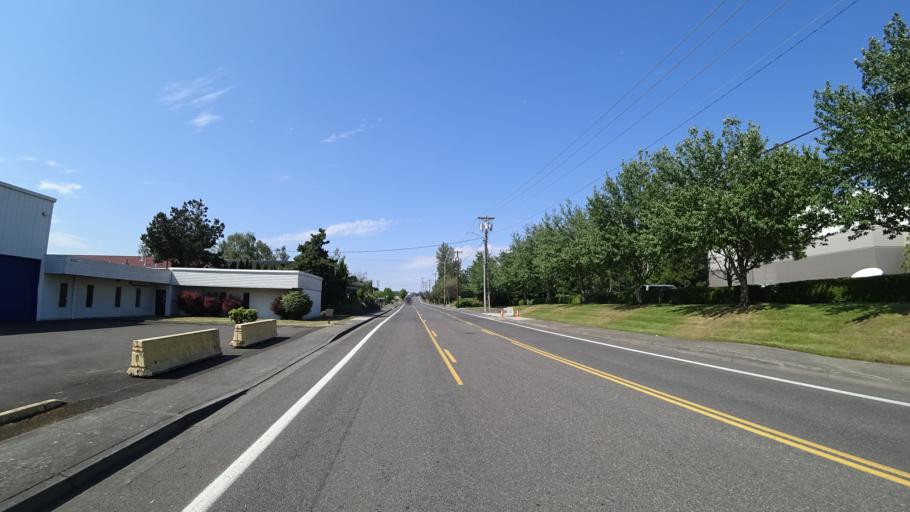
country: US
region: Oregon
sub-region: Multnomah County
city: Fairview
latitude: 45.5600
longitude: -122.5103
